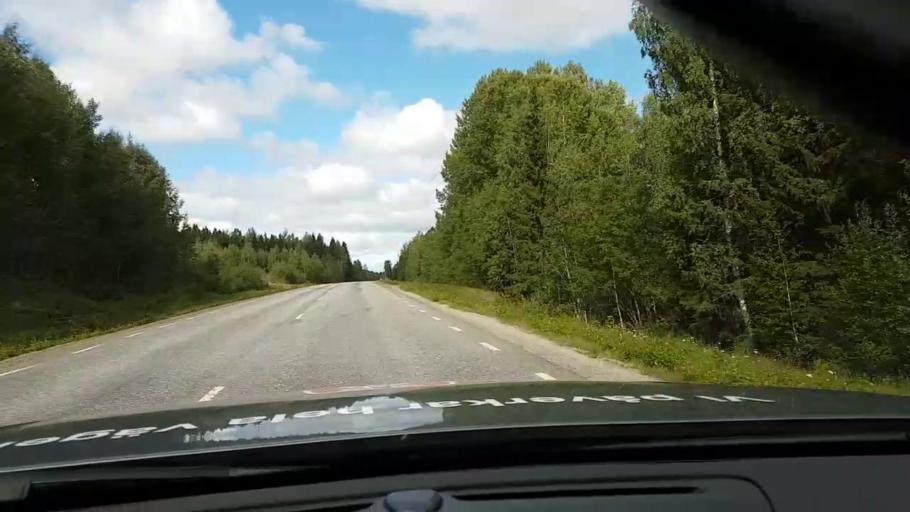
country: SE
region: Vaesternorrland
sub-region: OErnskoeldsviks Kommun
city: Bredbyn
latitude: 63.4722
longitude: 18.0984
